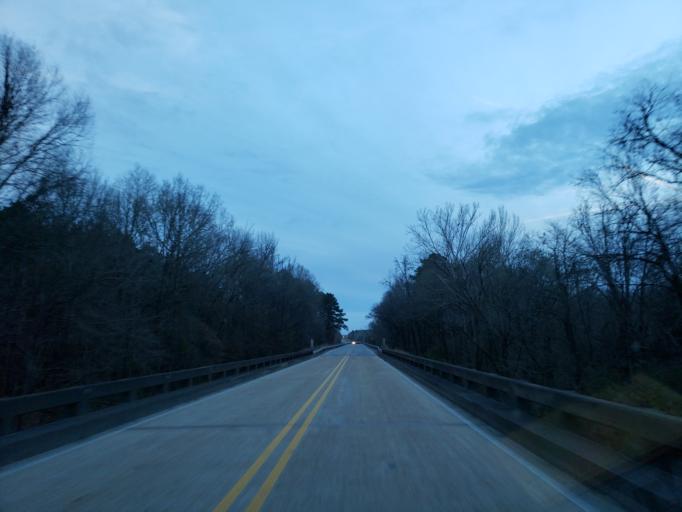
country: US
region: Alabama
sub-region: Sumter County
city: Livingston
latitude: 32.8101
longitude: -88.3117
